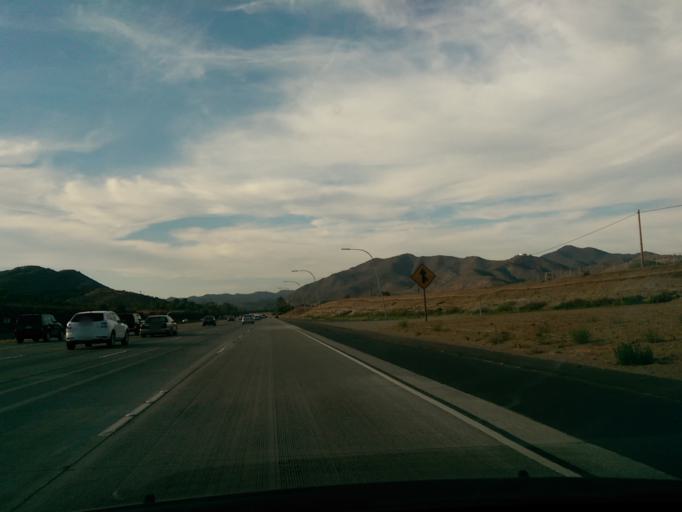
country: US
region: California
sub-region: San Diego County
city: Rainbow
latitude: 33.3335
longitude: -117.1590
